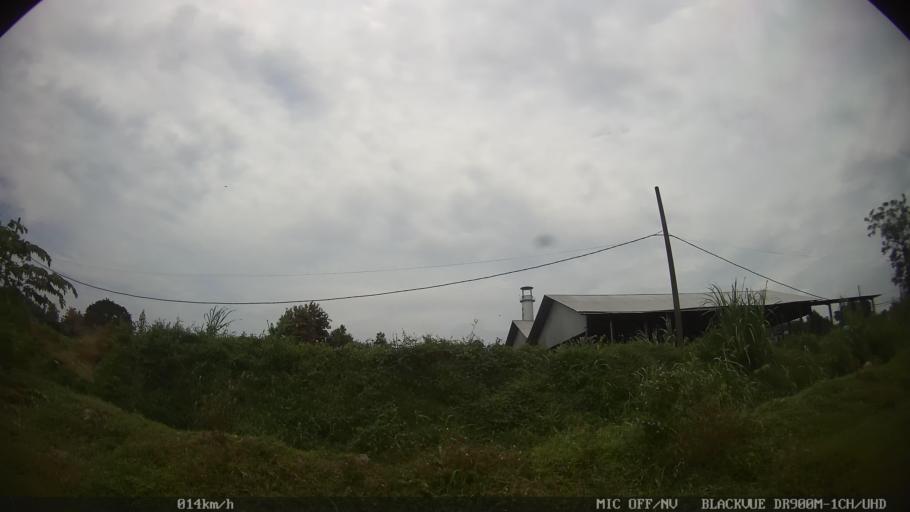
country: ID
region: North Sumatra
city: Sunggal
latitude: 3.6214
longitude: 98.5804
